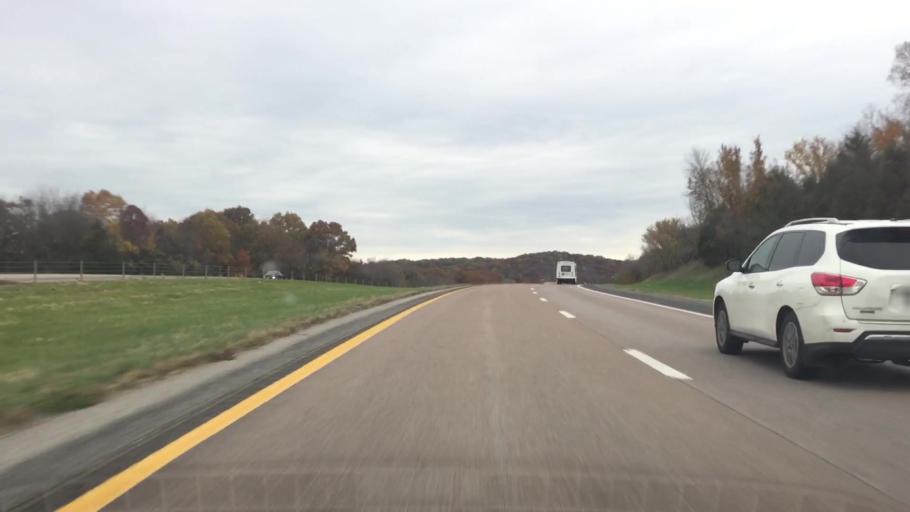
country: US
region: Missouri
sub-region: Cole County
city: Jefferson City
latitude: 38.6526
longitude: -92.2105
